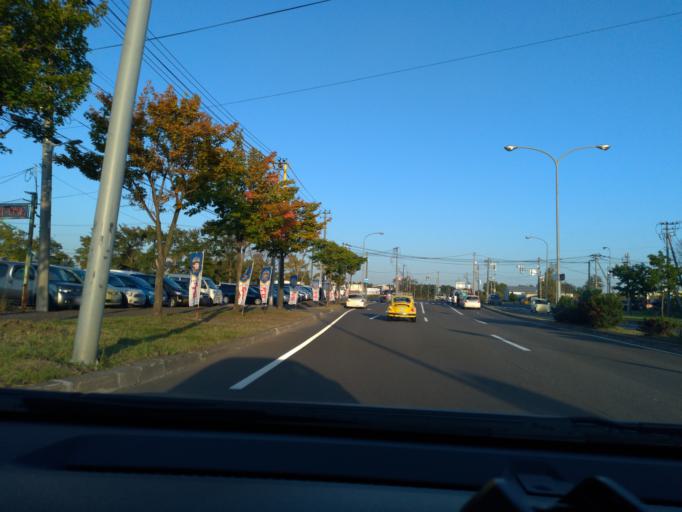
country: JP
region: Hokkaido
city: Ishikari
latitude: 43.1570
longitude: 141.4127
